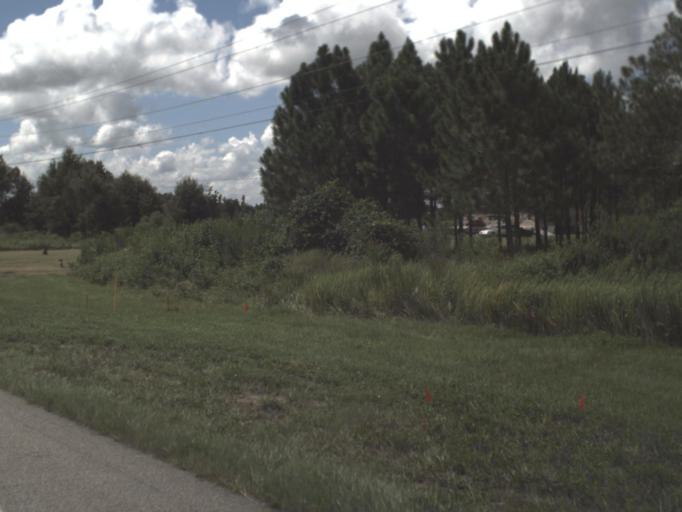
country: US
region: Florida
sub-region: Polk County
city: Polk City
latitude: 28.2600
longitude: -81.8252
